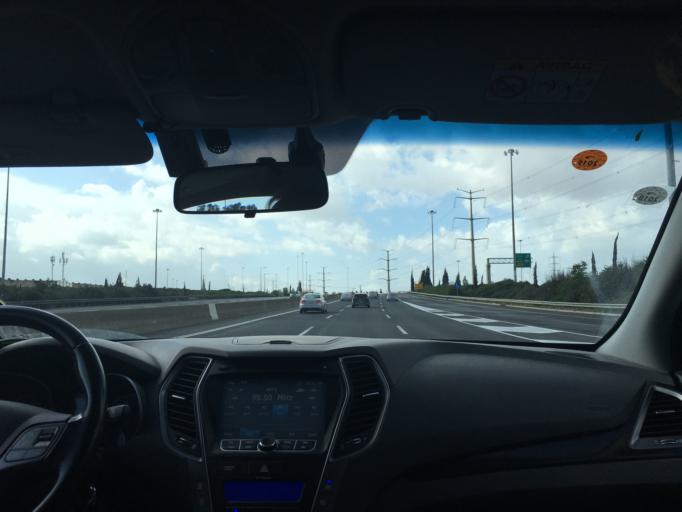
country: IL
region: Tel Aviv
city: Azor
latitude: 32.0146
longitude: 34.8183
